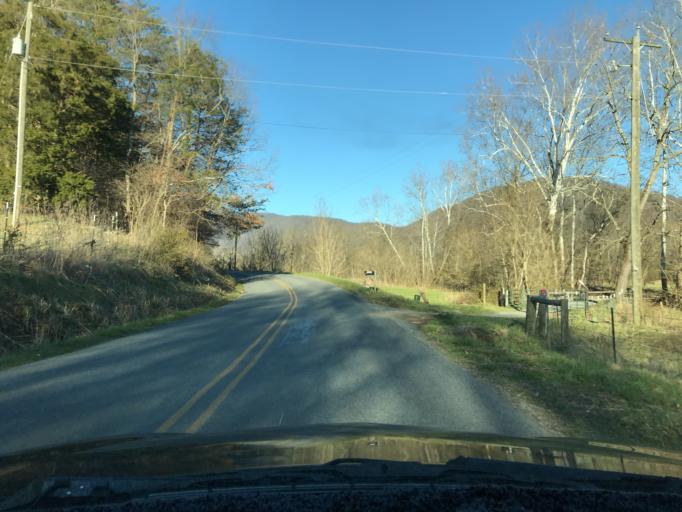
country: US
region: Virginia
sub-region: Botetourt County
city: Buchanan
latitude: 37.4299
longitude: -79.6842
